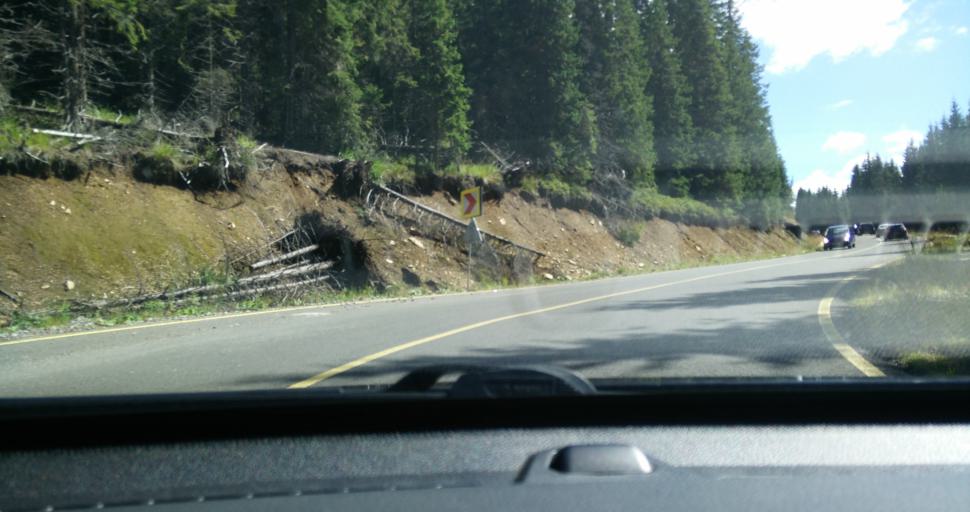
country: RO
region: Hunedoara
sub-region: Oras Petrila
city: Petrila
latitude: 45.4657
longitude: 23.6218
